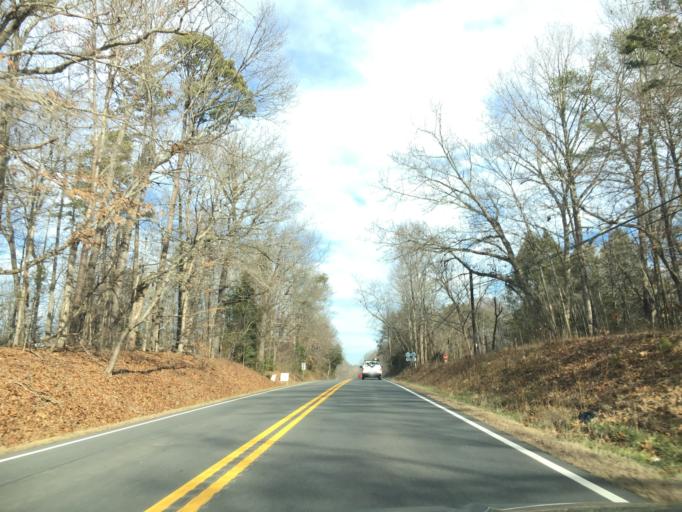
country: US
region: Virginia
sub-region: Culpeper County
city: Culpeper
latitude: 38.6074
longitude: -77.9542
